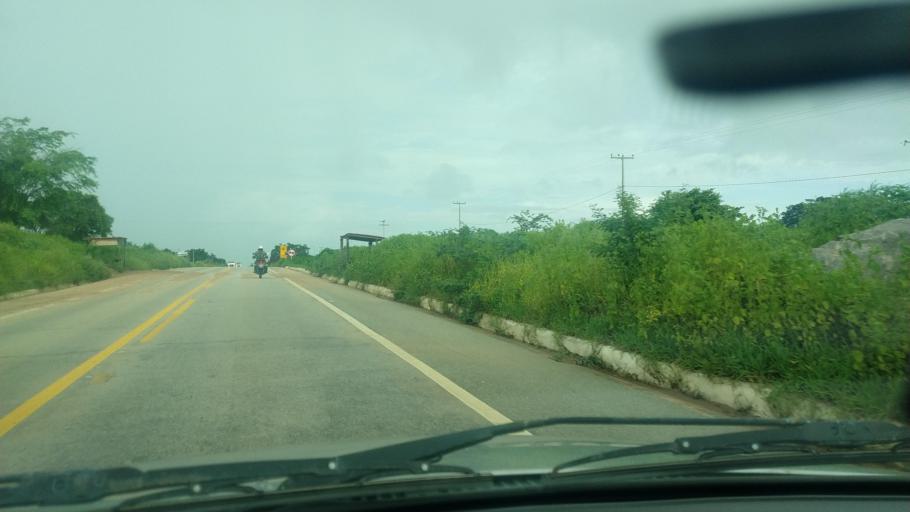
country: BR
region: Rio Grande do Norte
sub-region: Santa Cruz
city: Santa Cruz
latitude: -6.2004
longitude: -36.1977
